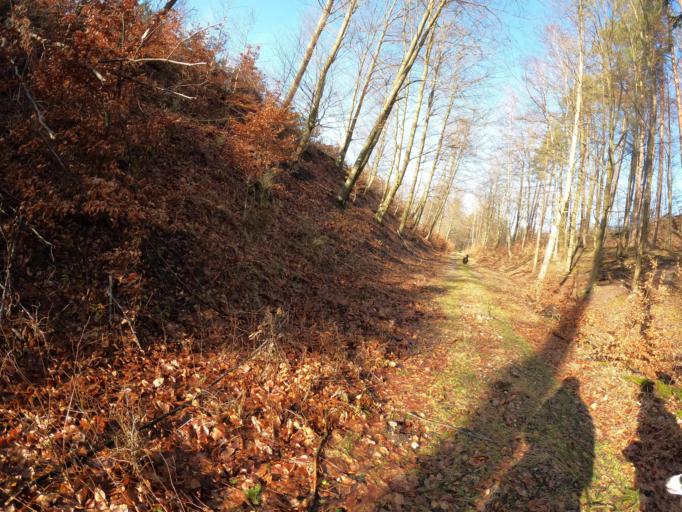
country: PL
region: West Pomeranian Voivodeship
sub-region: Powiat koszalinski
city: Polanow
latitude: 54.2063
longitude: 16.7209
